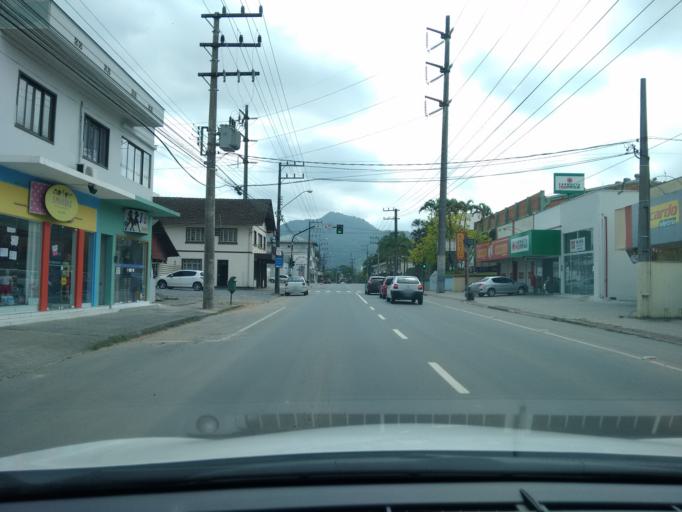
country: BR
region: Santa Catarina
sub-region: Jaragua Do Sul
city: Jaragua do Sul
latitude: -26.5127
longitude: -49.1202
